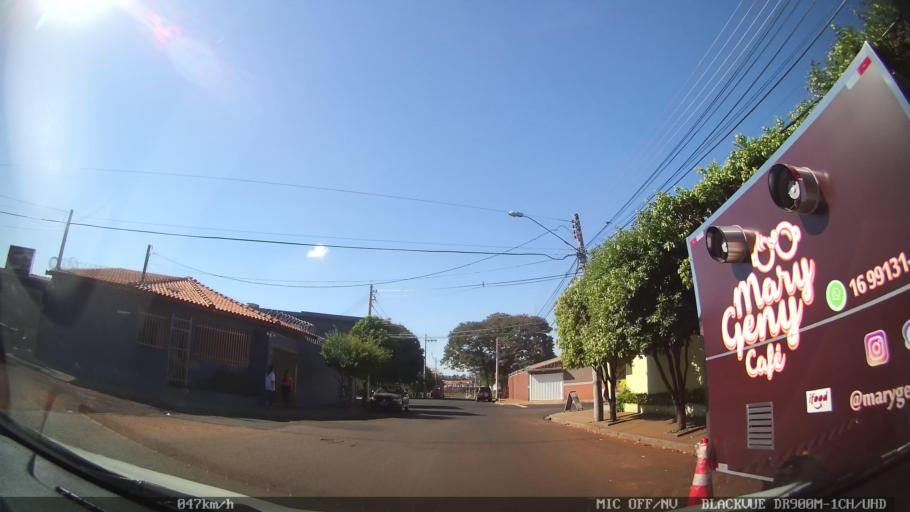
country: BR
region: Sao Paulo
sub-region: Ribeirao Preto
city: Ribeirao Preto
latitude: -21.2176
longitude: -47.7637
